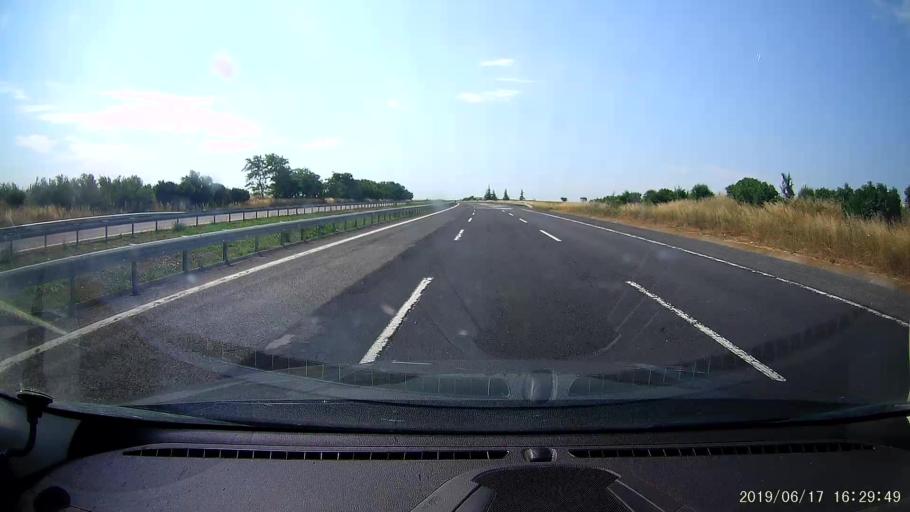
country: TR
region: Tekirdag
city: Beyazkoy
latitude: 41.3388
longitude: 27.6715
